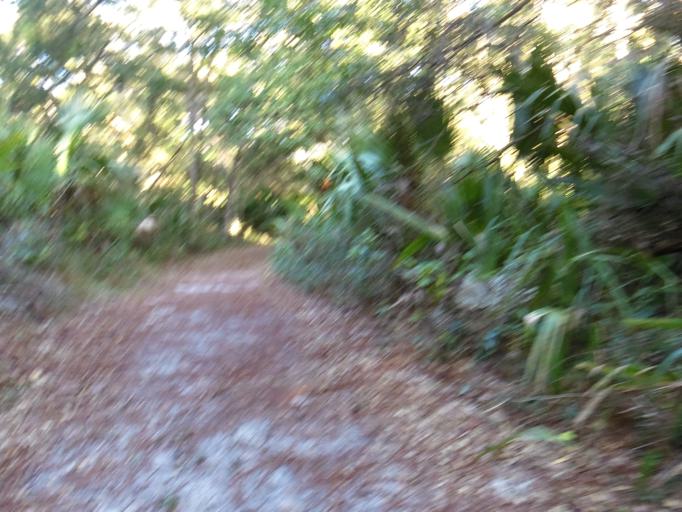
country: US
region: Florida
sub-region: Duval County
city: Atlantic Beach
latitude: 30.4759
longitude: -81.4180
